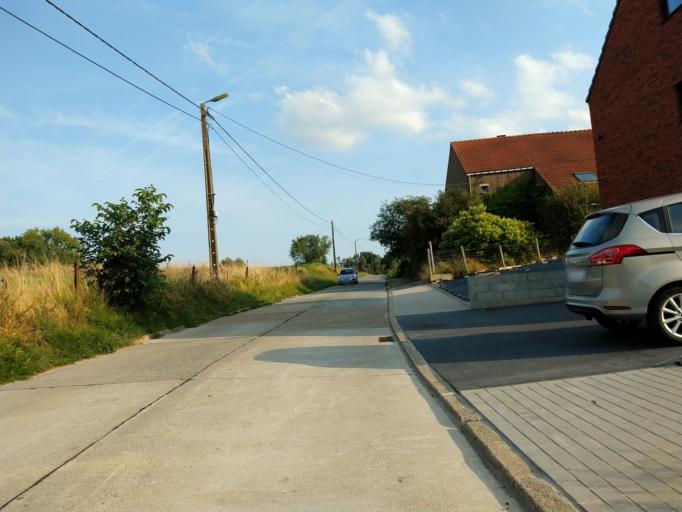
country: BE
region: Flanders
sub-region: Provincie Vlaams-Brabant
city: Boutersem
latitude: 50.8186
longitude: 4.8126
